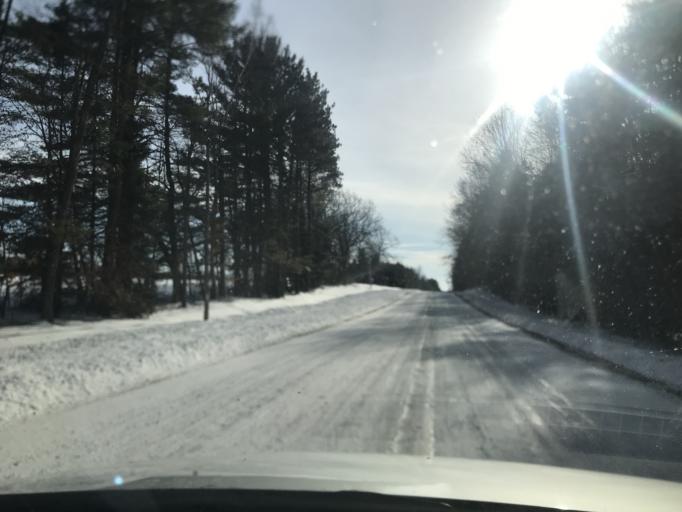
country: US
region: Wisconsin
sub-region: Oconto County
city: Gillett
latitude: 45.1328
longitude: -88.2497
